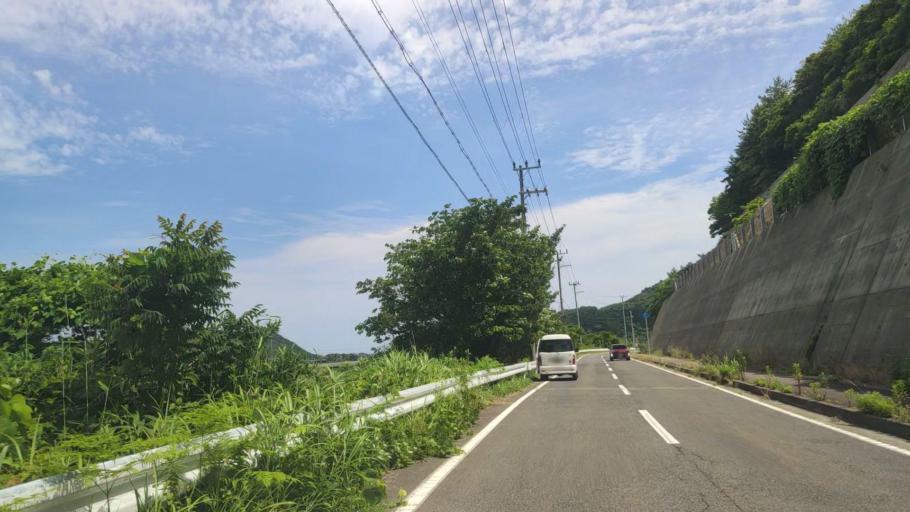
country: JP
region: Hyogo
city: Toyooka
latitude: 35.6443
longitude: 134.7622
